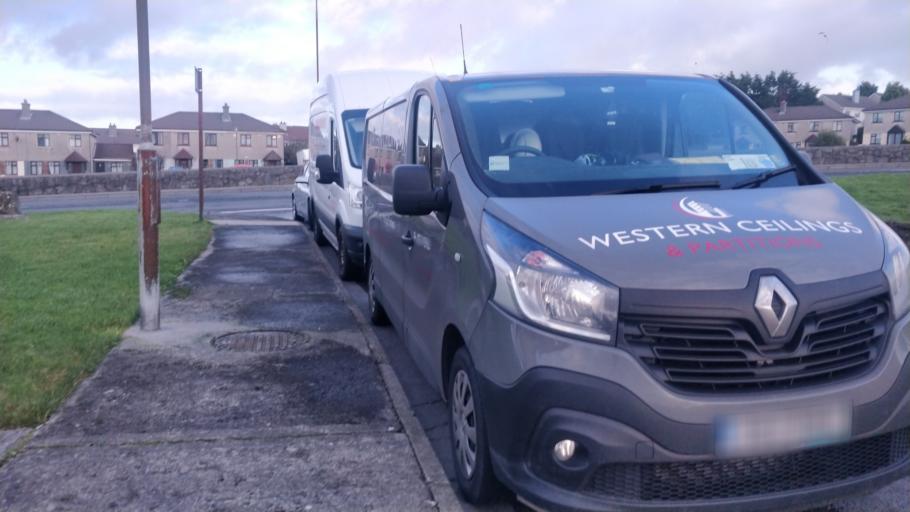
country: IE
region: Connaught
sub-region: County Galway
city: Gaillimh
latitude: 53.2865
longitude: -9.0032
